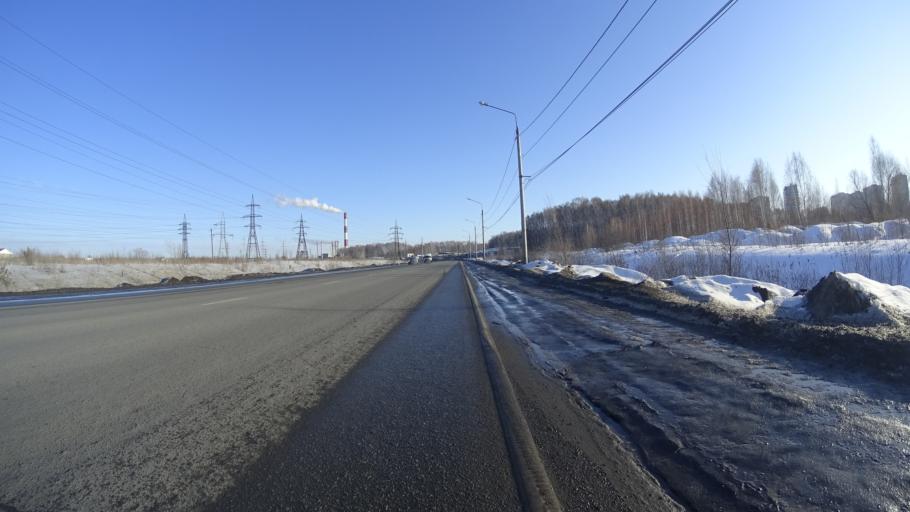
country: RU
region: Chelyabinsk
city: Roshchino
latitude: 55.2130
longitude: 61.3068
